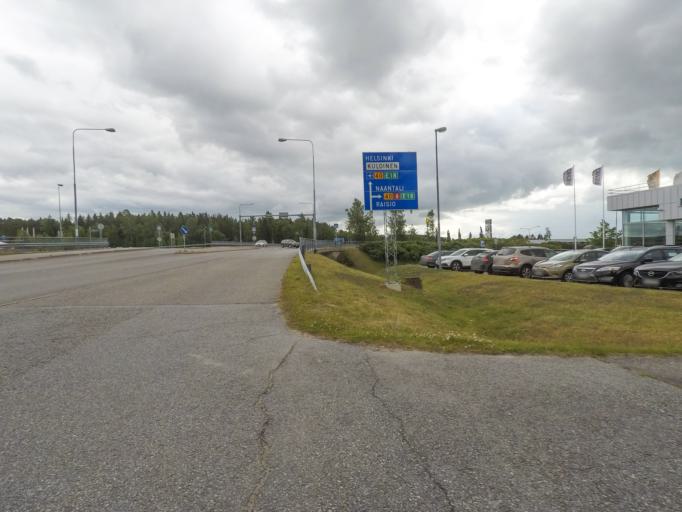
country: FI
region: Varsinais-Suomi
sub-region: Turku
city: Raisio
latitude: 60.4916
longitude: 22.1893
